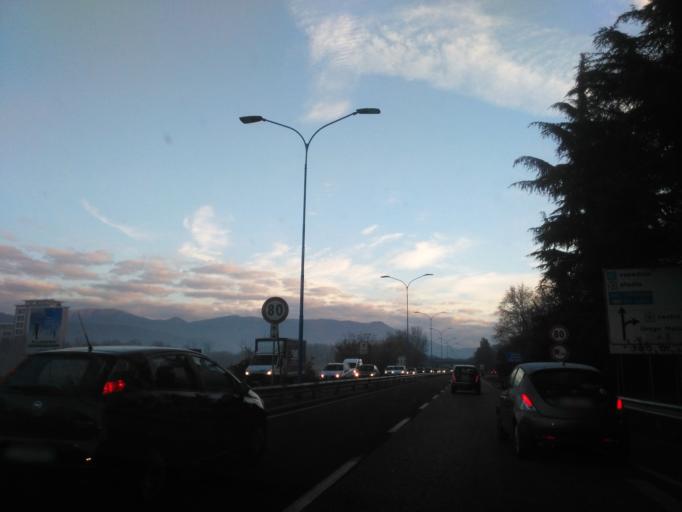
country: IT
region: Lombardy
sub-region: Provincia di Brescia
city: Fantasina
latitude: 45.5490
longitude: 10.1903
